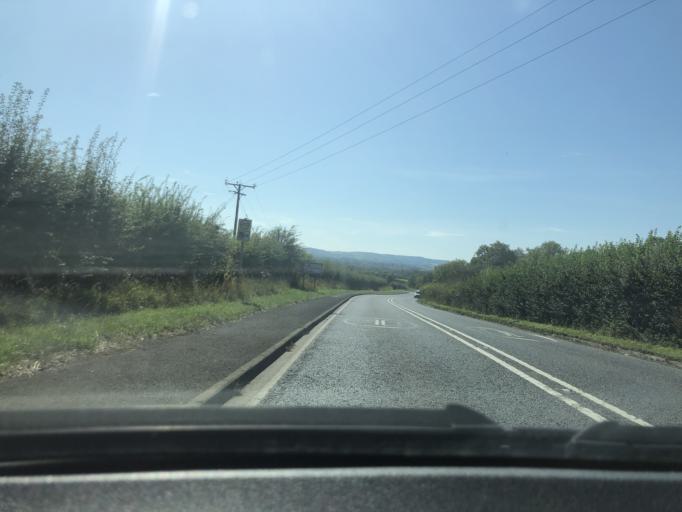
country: GB
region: England
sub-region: Somerset
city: Woolavington
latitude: 51.1560
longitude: -2.9409
